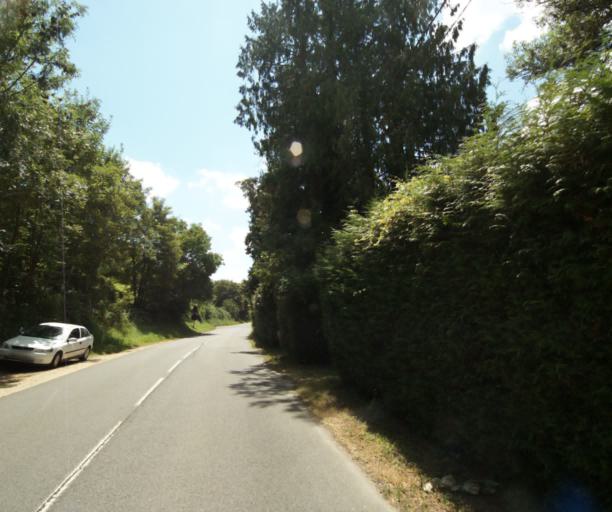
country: FR
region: Ile-de-France
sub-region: Departement de Seine-et-Marne
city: Hericy
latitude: 48.4596
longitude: 2.7717
